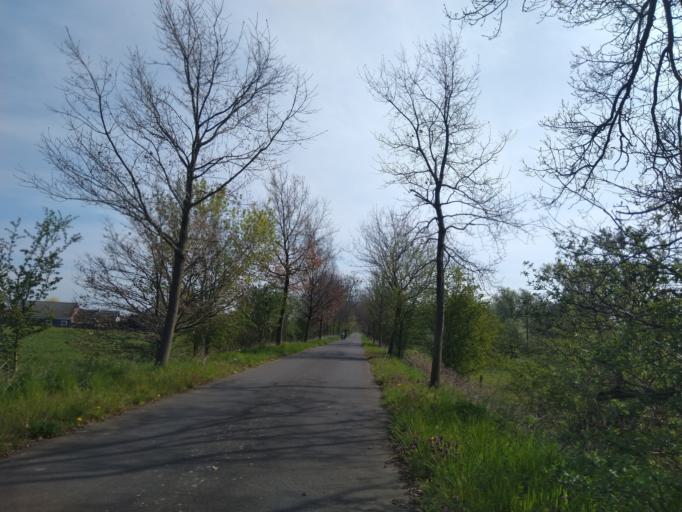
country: DE
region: Brandenburg
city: Bliesdorf
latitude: 52.7245
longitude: 14.1756
